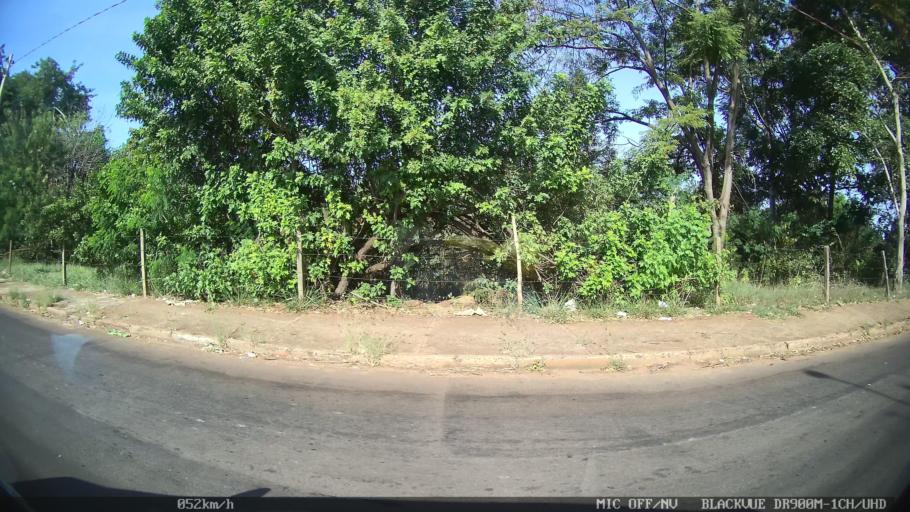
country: BR
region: Sao Paulo
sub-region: Sao Jose Do Rio Preto
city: Sao Jose do Rio Preto
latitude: -20.7854
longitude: -49.3846
